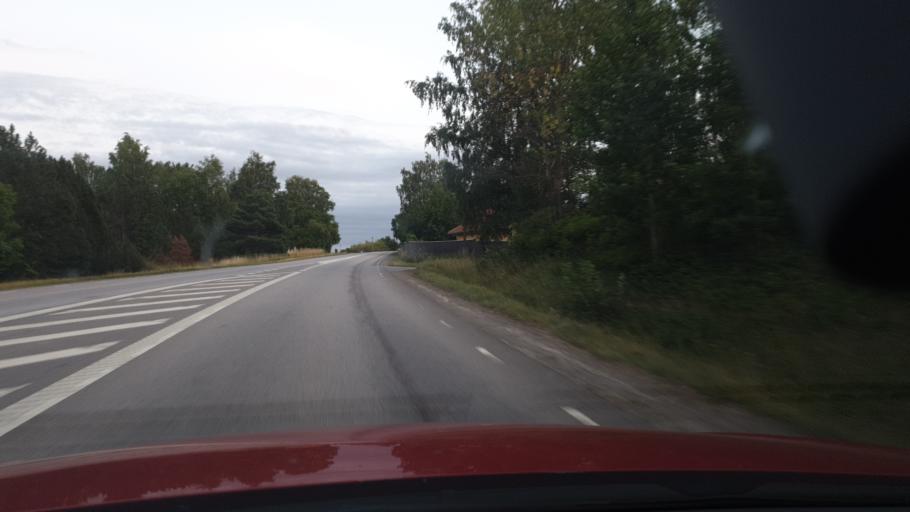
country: SE
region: Uppsala
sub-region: Habo Kommun
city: Balsta
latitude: 59.6042
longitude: 17.5068
